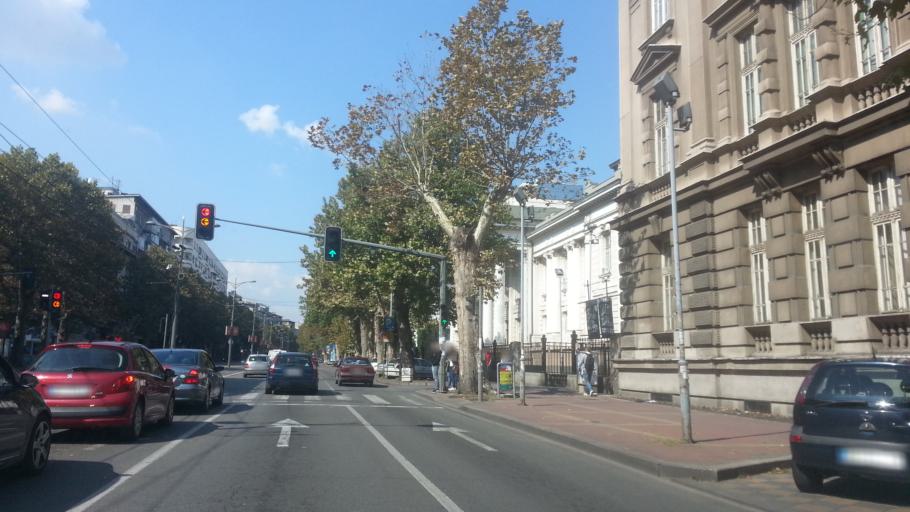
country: RS
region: Central Serbia
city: Belgrade
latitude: 44.8055
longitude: 20.4754
